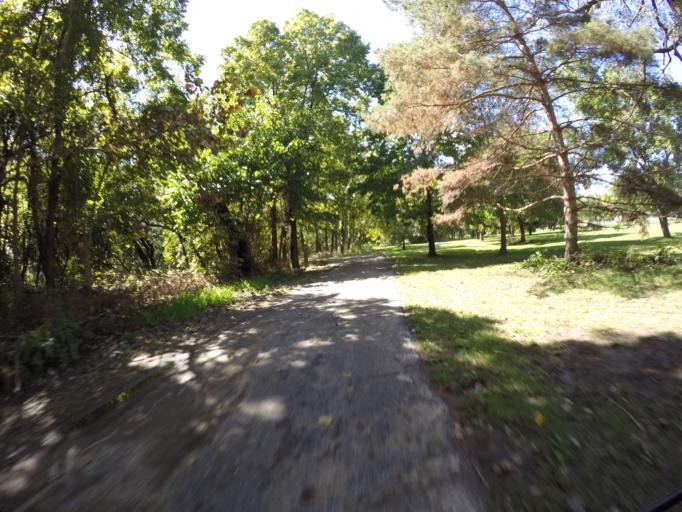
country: US
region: Kansas
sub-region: Johnson County
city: Olathe
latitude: 38.8910
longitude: -94.7658
